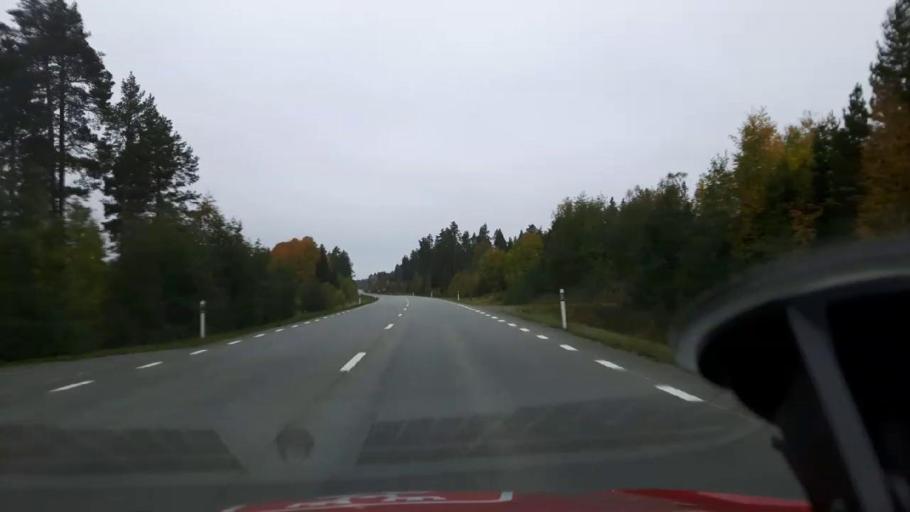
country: SE
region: Jaemtland
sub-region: Bergs Kommun
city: Hoverberg
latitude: 62.6745
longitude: 14.3830
